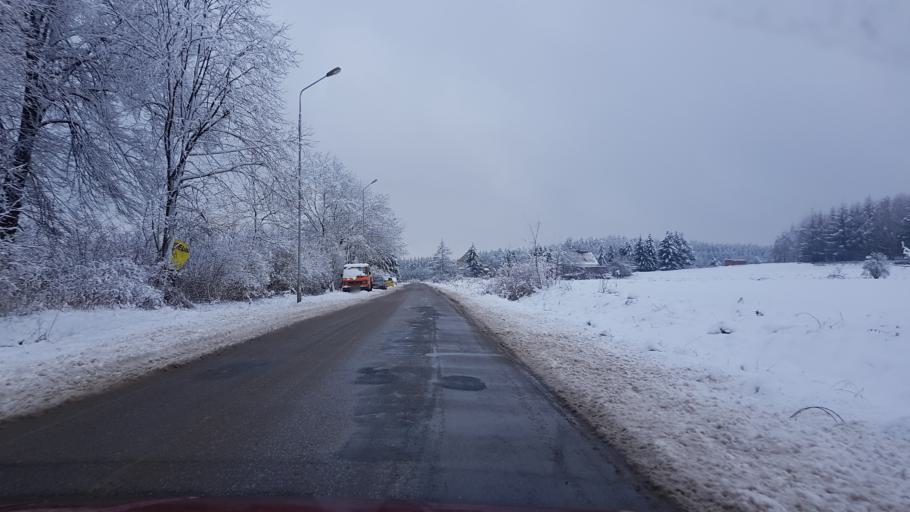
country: PL
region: West Pomeranian Voivodeship
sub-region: Powiat drawski
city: Zlocieniec
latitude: 53.5243
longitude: 16.0074
